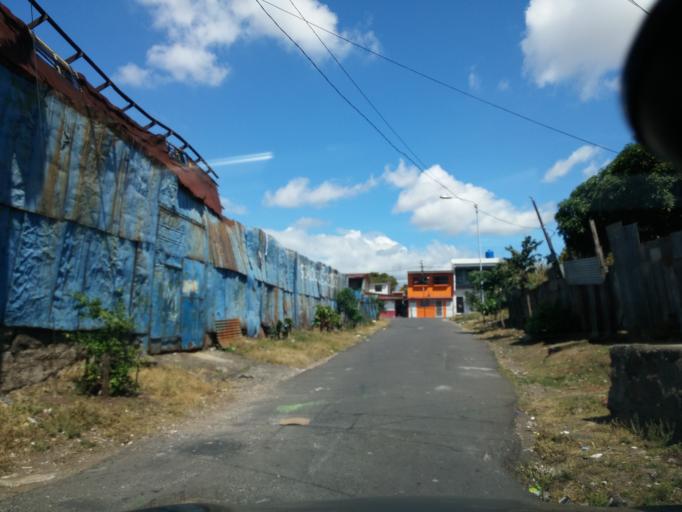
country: CR
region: San Jose
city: San Jose
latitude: 9.9223
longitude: -84.0921
